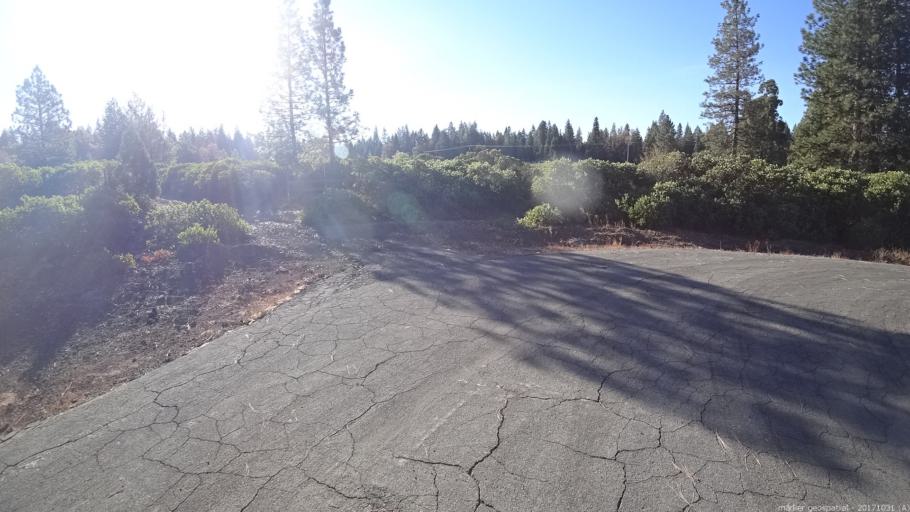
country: US
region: California
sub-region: Shasta County
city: Shingletown
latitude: 40.5248
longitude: -121.8329
